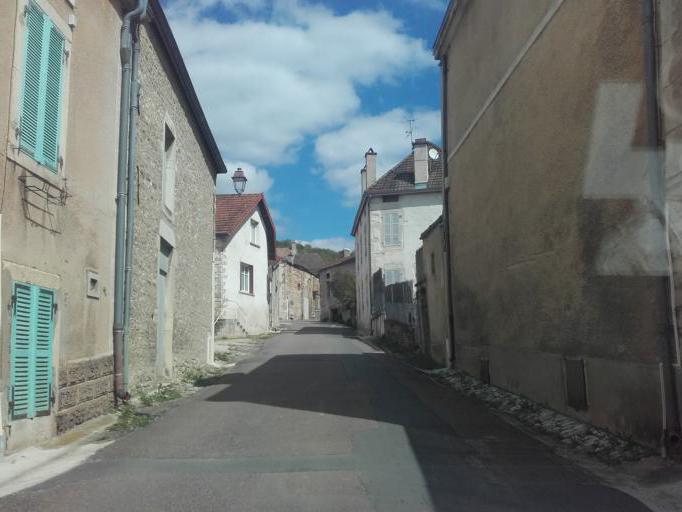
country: FR
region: Bourgogne
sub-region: Departement de la Cote-d'Or
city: Meursault
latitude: 46.9975
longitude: 4.7086
